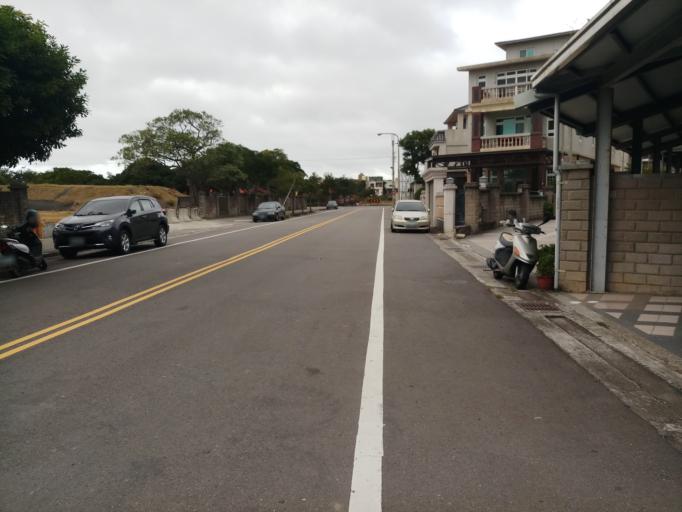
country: TW
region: Taiwan
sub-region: Miaoli
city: Miaoli
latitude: 24.6781
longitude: 120.8650
